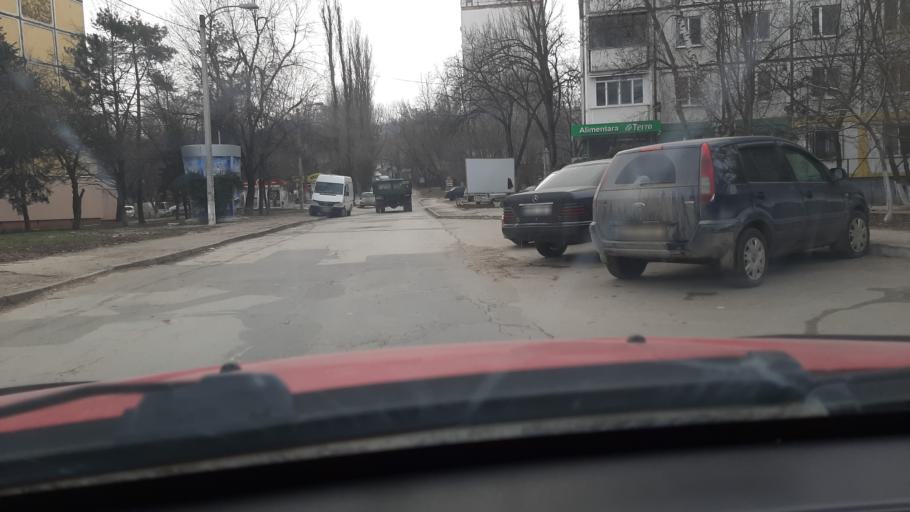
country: MD
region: Chisinau
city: Vatra
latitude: 47.0456
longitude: 28.7834
